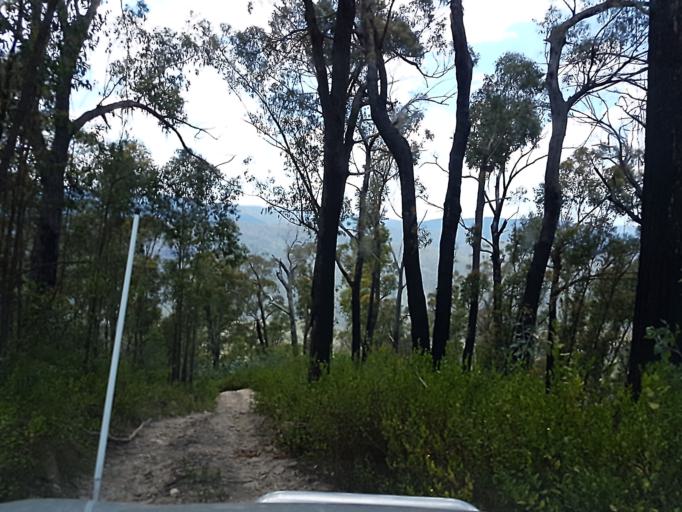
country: AU
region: Victoria
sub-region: East Gippsland
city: Lakes Entrance
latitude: -37.3472
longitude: 148.3454
